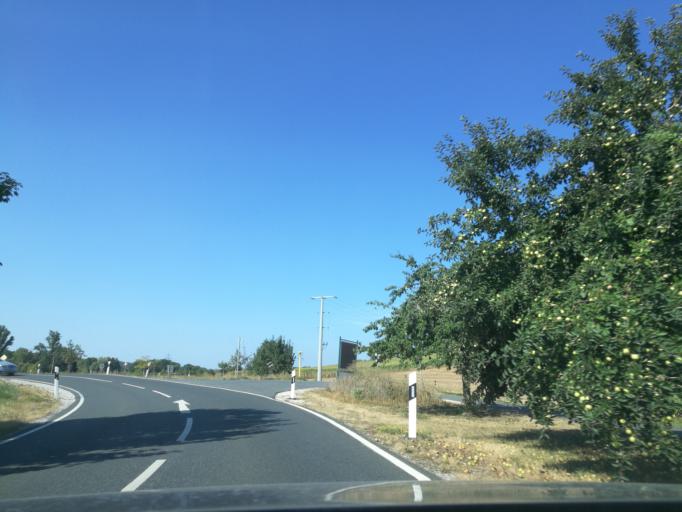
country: DE
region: Bavaria
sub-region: Regierungsbezirk Mittelfranken
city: Ammerndorf
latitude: 49.4192
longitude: 10.8452
